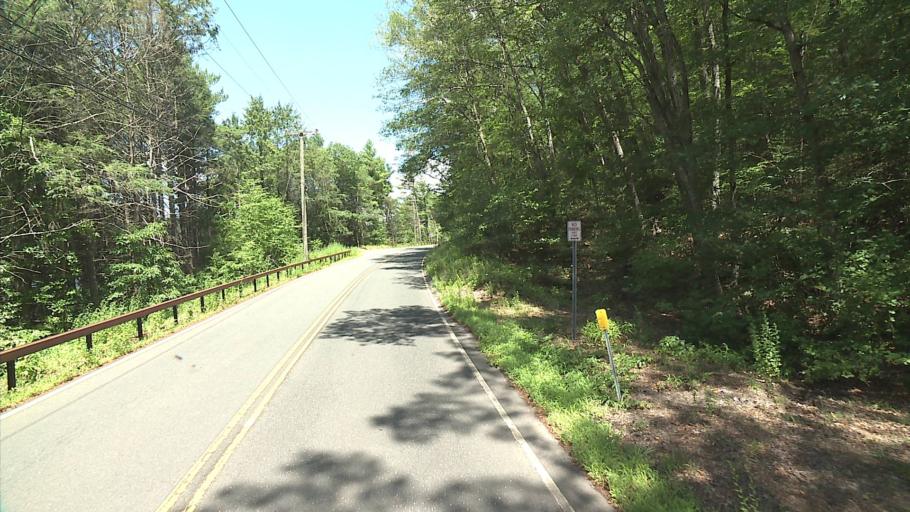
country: US
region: Connecticut
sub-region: Litchfield County
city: New Hartford Center
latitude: 41.9014
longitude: -72.9580
